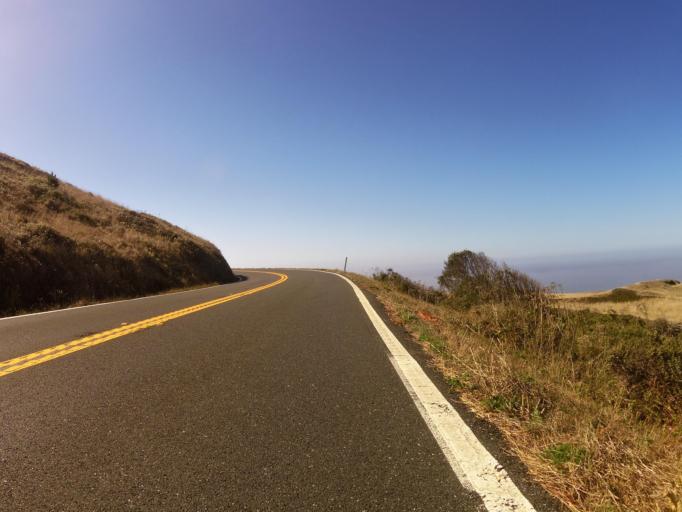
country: US
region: California
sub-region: Mendocino County
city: Fort Bragg
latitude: 39.1979
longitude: -123.7668
